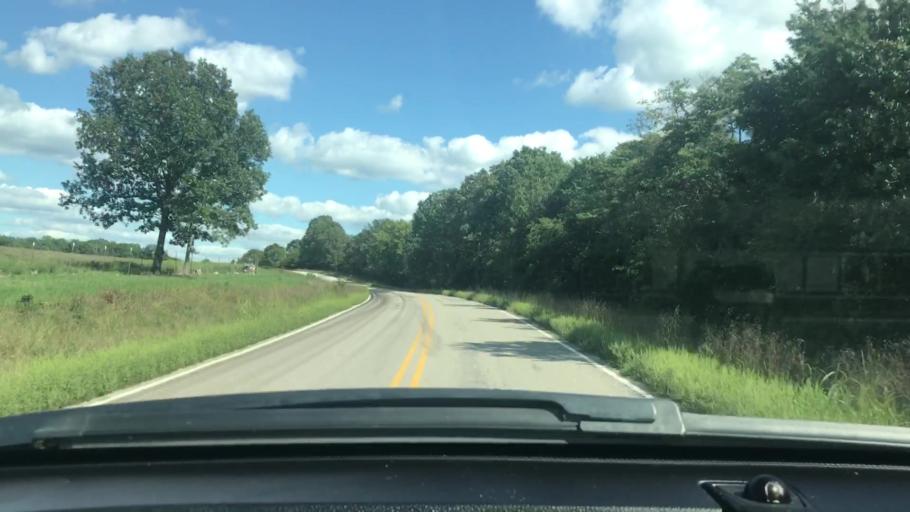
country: US
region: Missouri
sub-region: Wright County
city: Hartville
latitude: 37.3778
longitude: -92.4329
